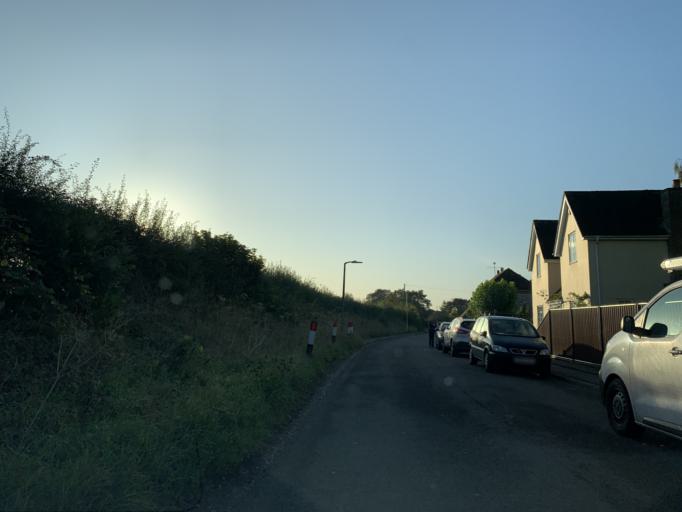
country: GB
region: England
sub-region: Wiltshire
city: Salisbury
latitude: 51.0910
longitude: -1.8136
